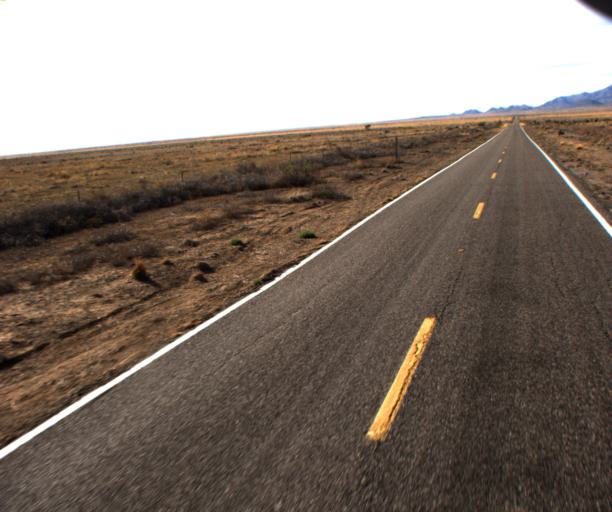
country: US
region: Arizona
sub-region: Cochise County
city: Willcox
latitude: 32.0638
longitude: -109.5047
